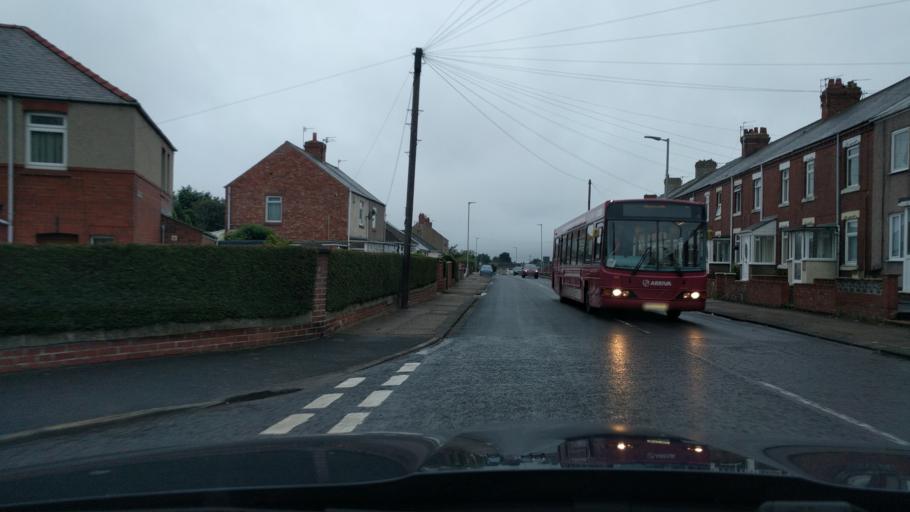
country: GB
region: England
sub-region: Northumberland
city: Bedlington
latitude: 55.1332
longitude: -1.5837
